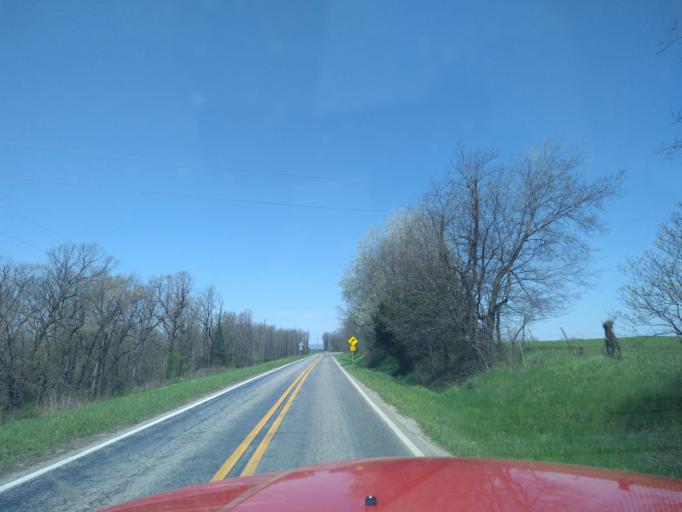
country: US
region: Arkansas
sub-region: Washington County
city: West Fork
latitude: 35.8773
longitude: -94.2417
